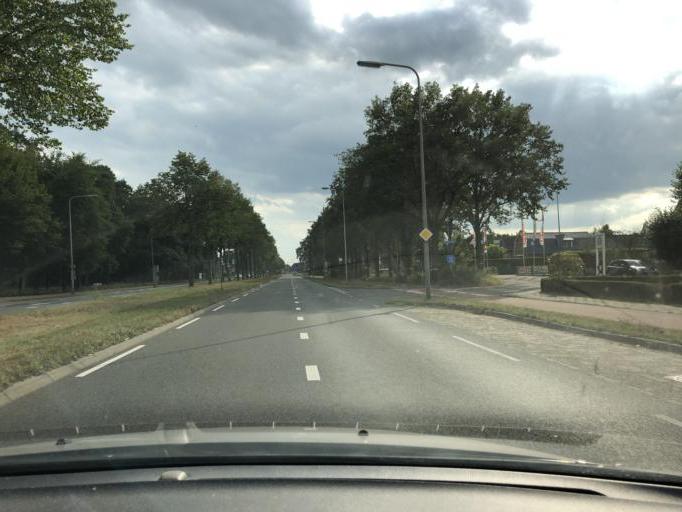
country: NL
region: Overijssel
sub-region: Gemeente Hardenberg
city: Hardenberg
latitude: 52.6247
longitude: 6.5570
